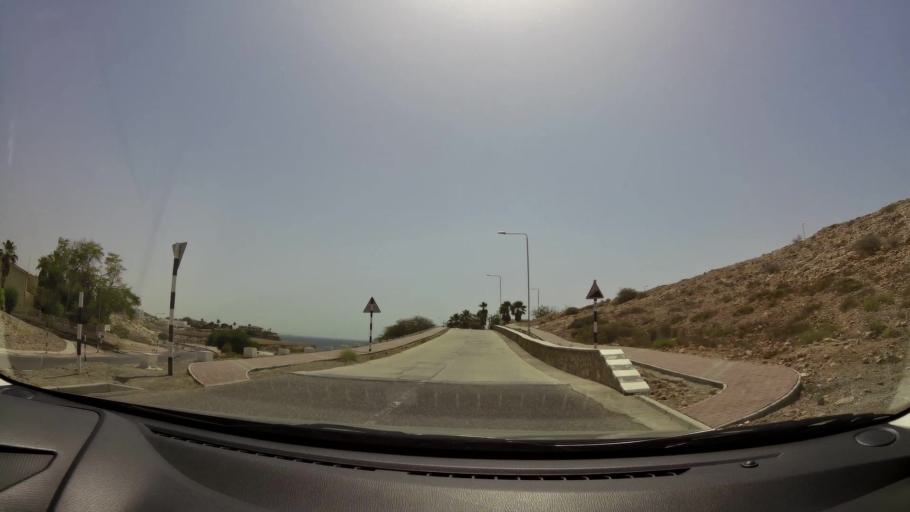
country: OM
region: Muhafazat Masqat
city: Muscat
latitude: 23.6400
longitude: 58.4936
